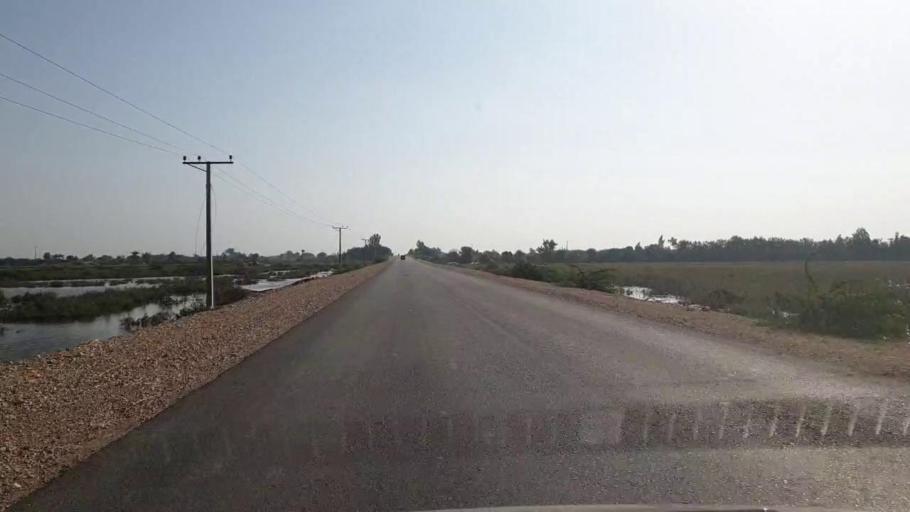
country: PK
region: Sindh
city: Badin
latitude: 24.6581
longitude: 68.9684
